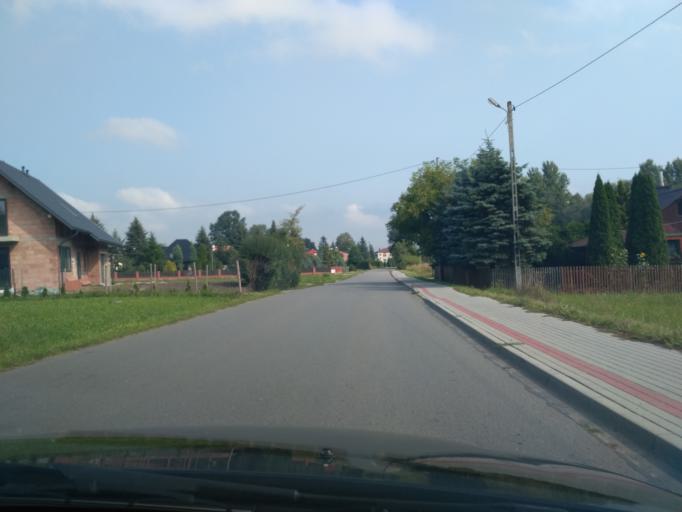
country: PL
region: Subcarpathian Voivodeship
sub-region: Powiat rzeszowski
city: Niechobrz
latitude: 49.9870
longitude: 21.8751
